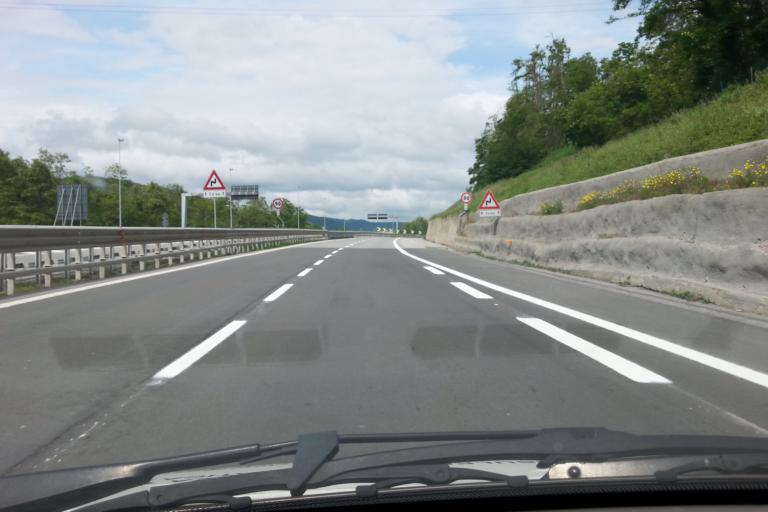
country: IT
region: Liguria
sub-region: Provincia di Savona
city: Altare
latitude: 44.3468
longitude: 8.3202
